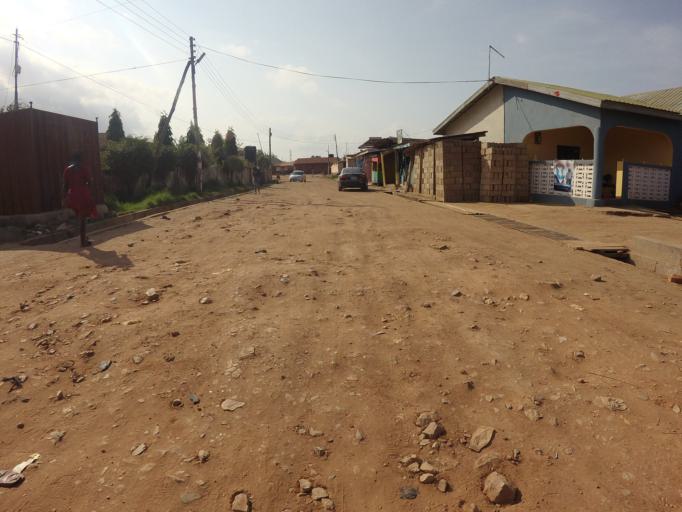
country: GH
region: Greater Accra
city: Dome
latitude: 5.6557
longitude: -0.2662
